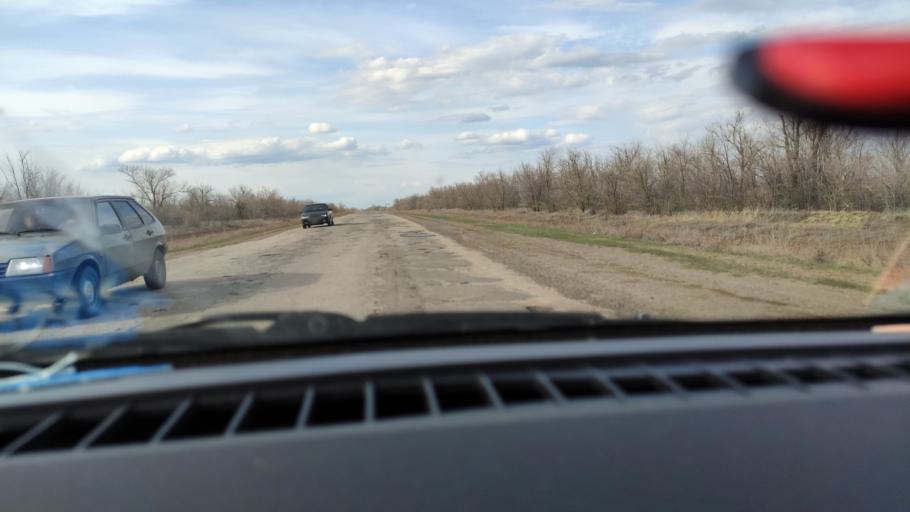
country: RU
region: Saratov
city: Rovnoye
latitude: 50.9704
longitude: 46.1170
